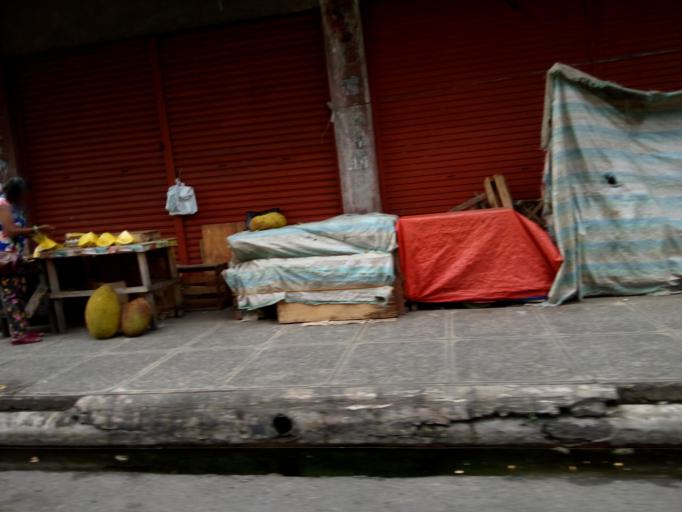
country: PH
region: Caraga
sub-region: Province of Surigao del Norte
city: Surigao
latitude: 9.7902
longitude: 125.4926
